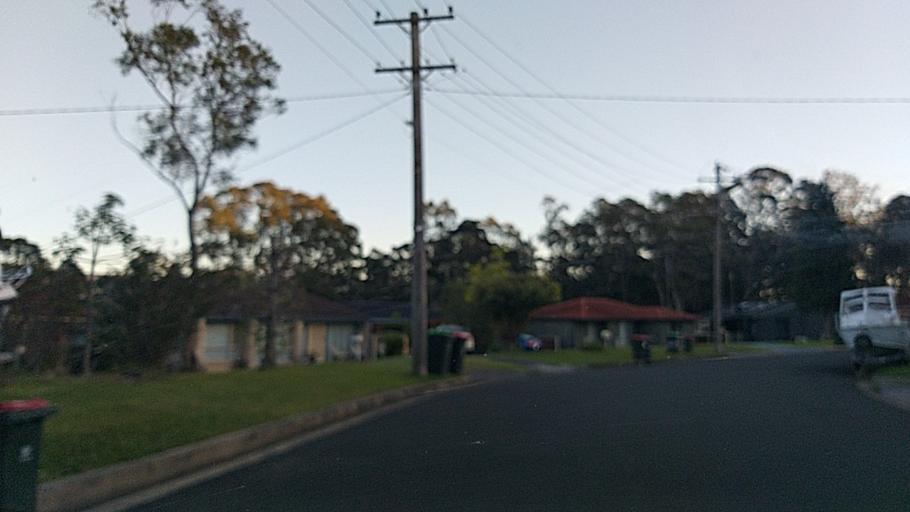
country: AU
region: New South Wales
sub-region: Wollongong
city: Dapto
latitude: -34.5096
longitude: 150.7828
